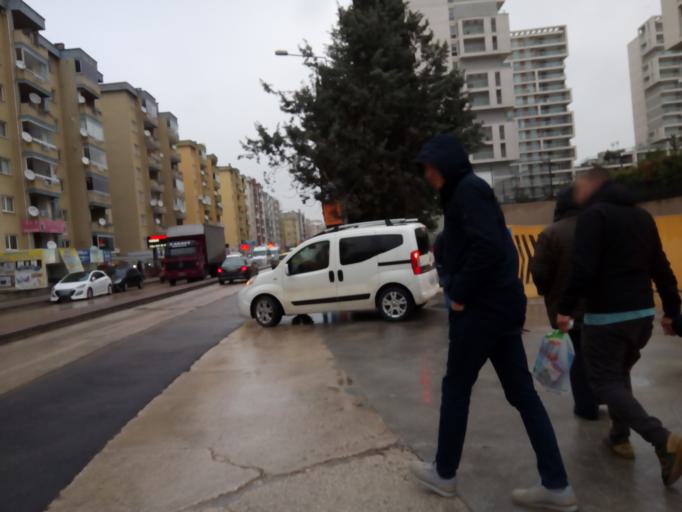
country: TR
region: Bursa
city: Niluefer
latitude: 40.2525
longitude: 28.9571
